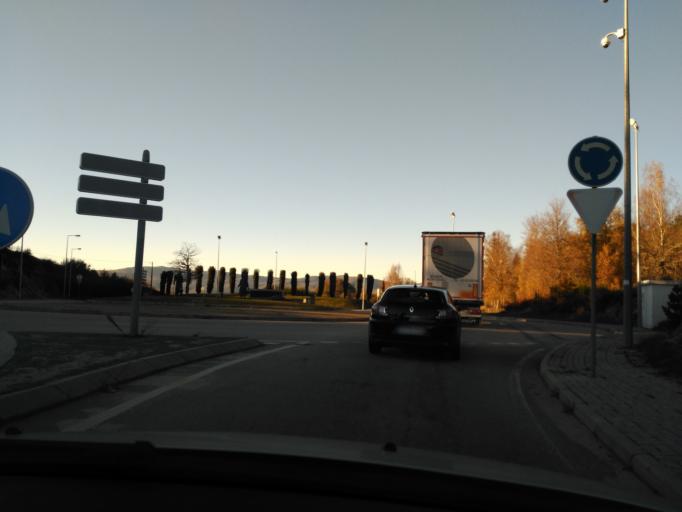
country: PT
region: Vila Real
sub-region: Montalegre
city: Montalegre
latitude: 41.8133
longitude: -7.7899
